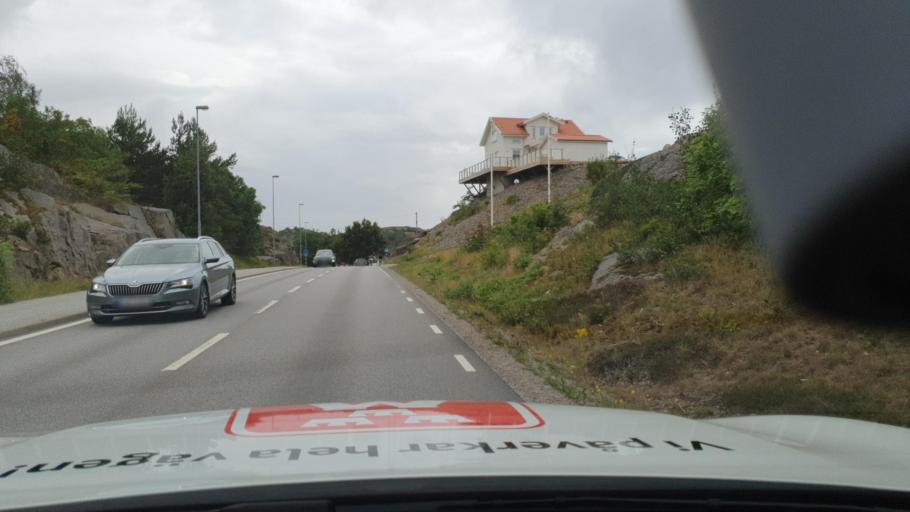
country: SE
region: Vaestra Goetaland
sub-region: Sotenas Kommun
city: Hunnebostrand
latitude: 58.4769
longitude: 11.3278
